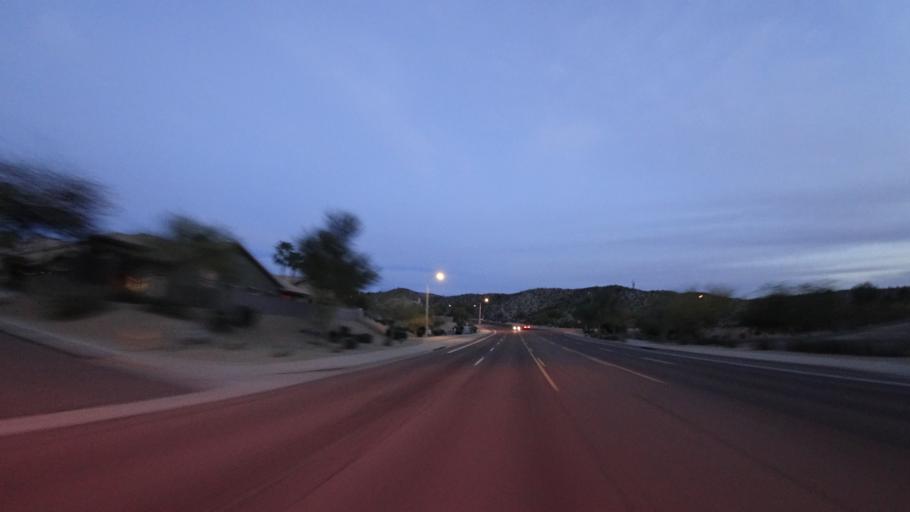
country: US
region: Arizona
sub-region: Maricopa County
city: Laveen
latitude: 33.3046
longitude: -112.0769
